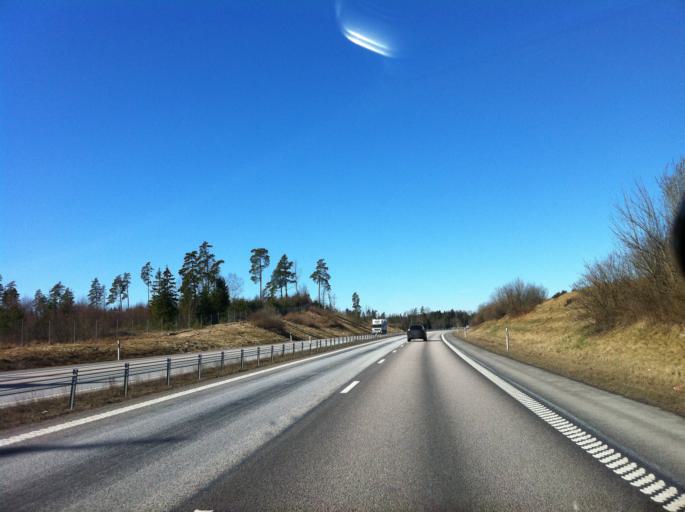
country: SE
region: Vaestra Goetaland
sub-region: Vanersborgs Kommun
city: Vanersborg
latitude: 58.3688
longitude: 12.3506
